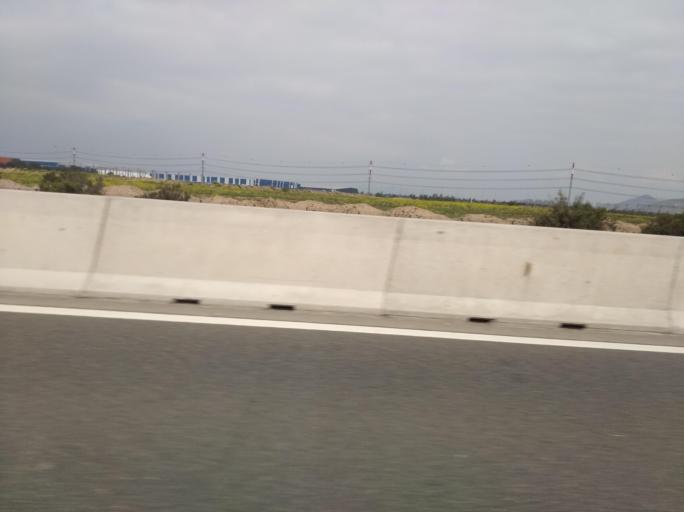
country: CL
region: Santiago Metropolitan
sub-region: Provincia de Santiago
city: Lo Prado
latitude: -33.4274
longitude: -70.8040
